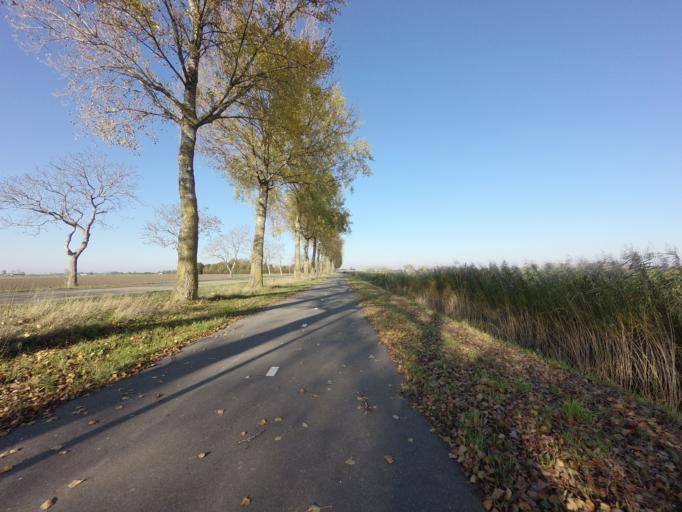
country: NL
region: North Brabant
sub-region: Gemeente Waalwijk
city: Waalwijk
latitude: 51.7212
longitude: 5.0568
